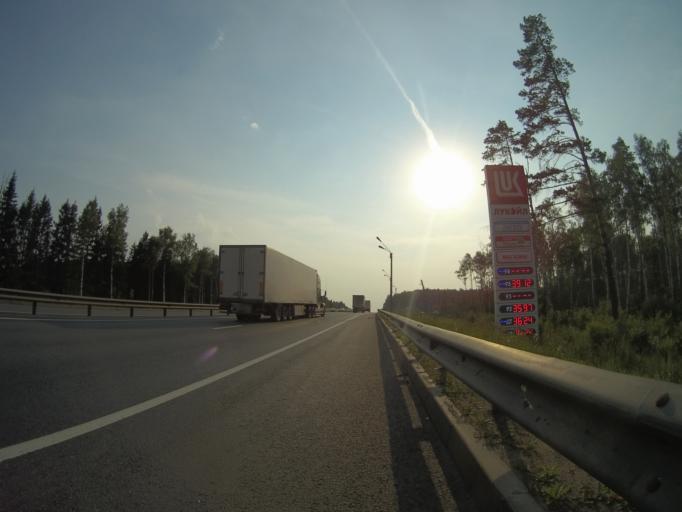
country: RU
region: Vladimir
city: Melekhovo
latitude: 56.2114
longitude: 41.3066
